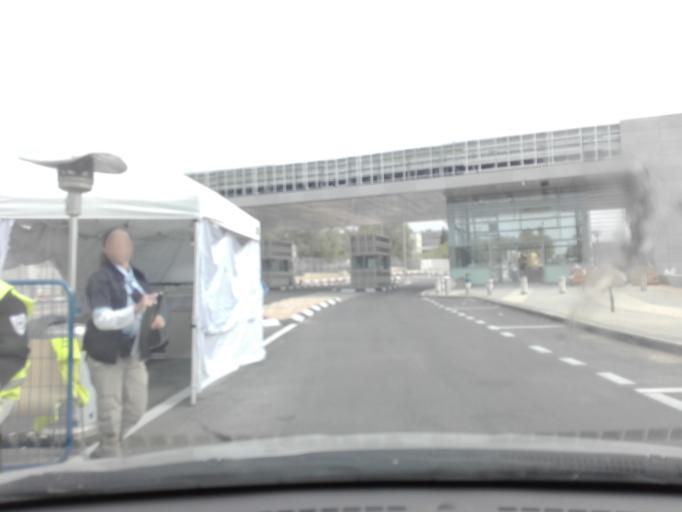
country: IL
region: Southern District
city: Beersheba
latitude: 31.2639
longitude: 34.7989
